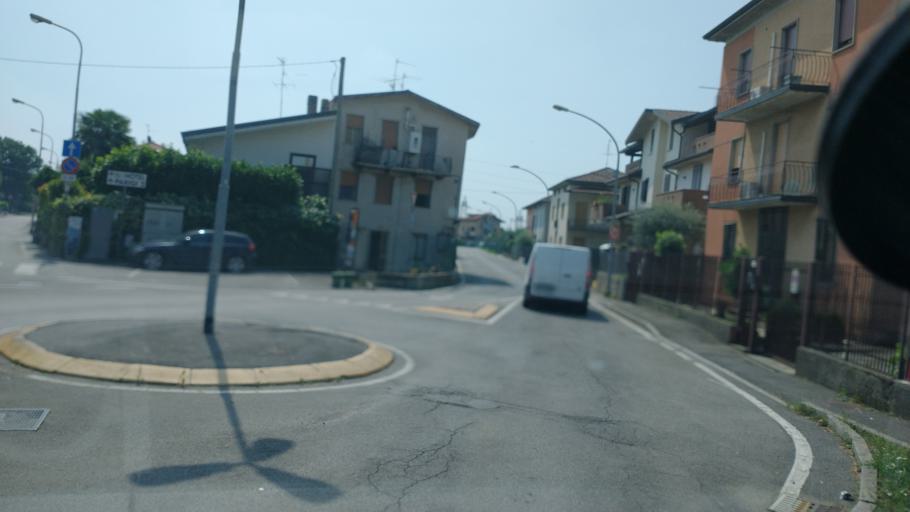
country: IT
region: Lombardy
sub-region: Provincia di Bergamo
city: Levate
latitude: 45.6373
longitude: 9.6166
